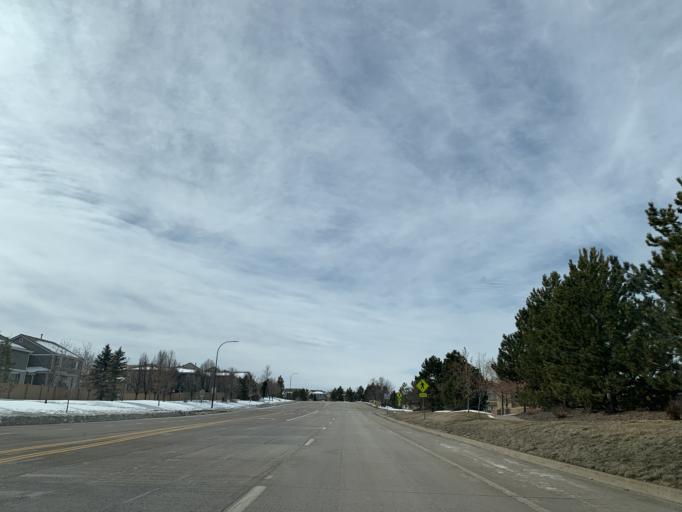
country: US
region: Colorado
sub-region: Douglas County
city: Carriage Club
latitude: 39.5251
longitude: -104.9394
